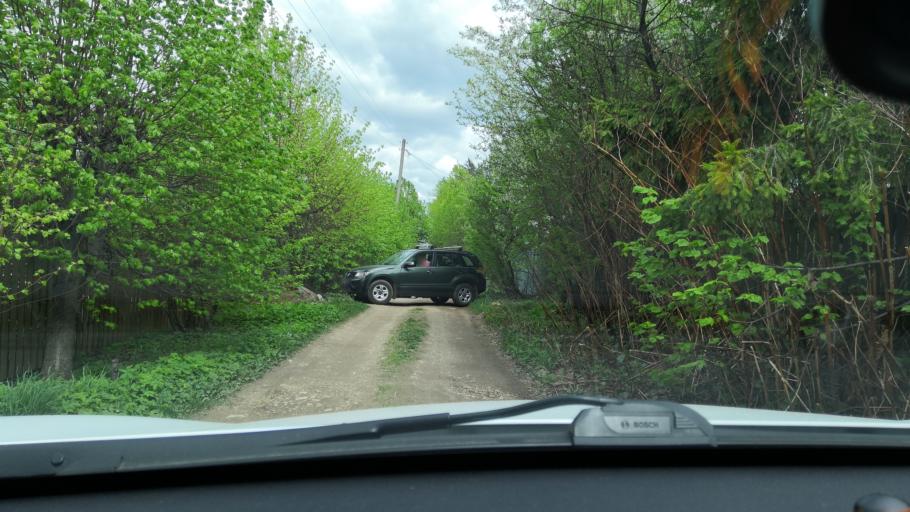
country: RU
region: Moskovskaya
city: Dedenevo
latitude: 56.2623
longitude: 37.5685
